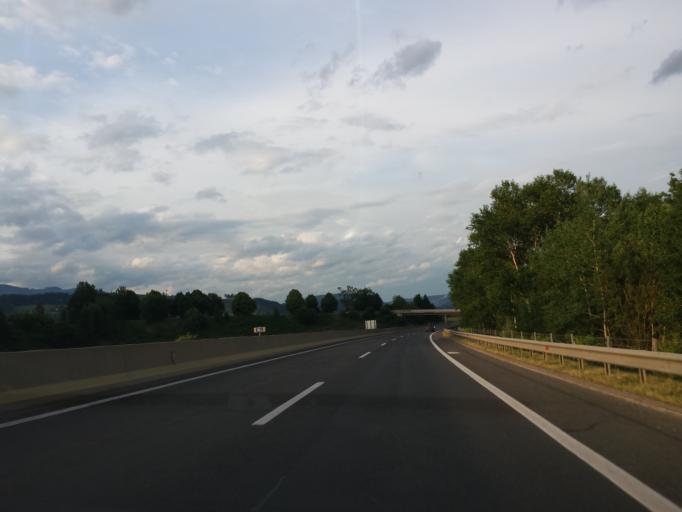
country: AT
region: Styria
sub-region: Politischer Bezirk Murtal
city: Kobenz
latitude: 47.2370
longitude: 14.8400
